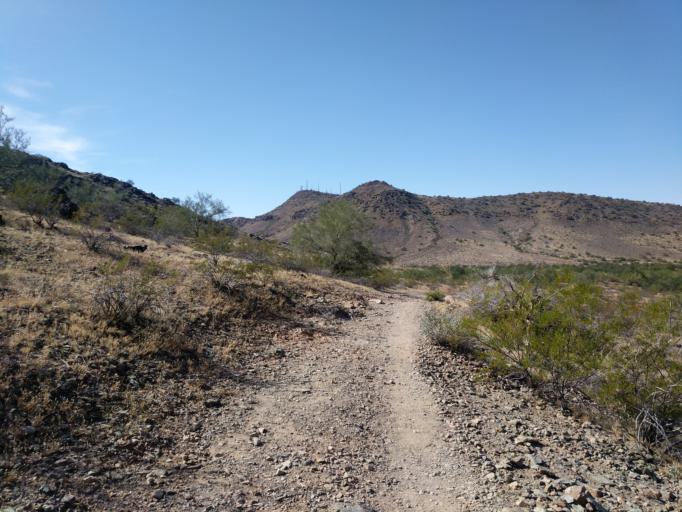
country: US
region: Arizona
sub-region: Maricopa County
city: Glendale
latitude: 33.5915
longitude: -112.0686
